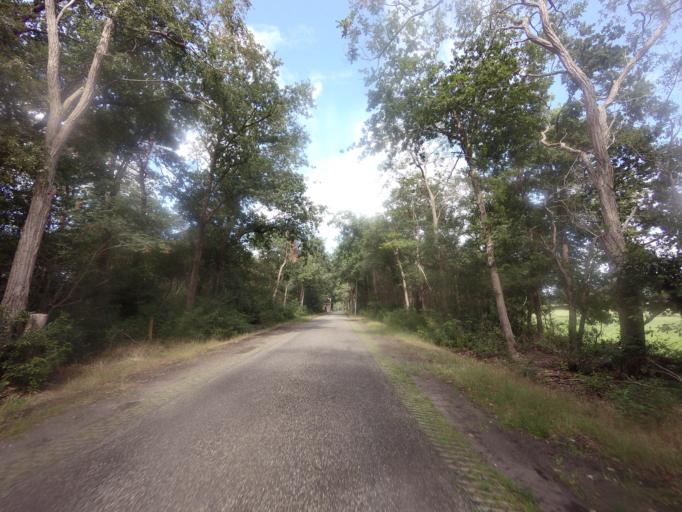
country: NL
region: Overijssel
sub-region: Gemeente Staphorst
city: Staphorst
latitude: 52.6614
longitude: 6.2641
